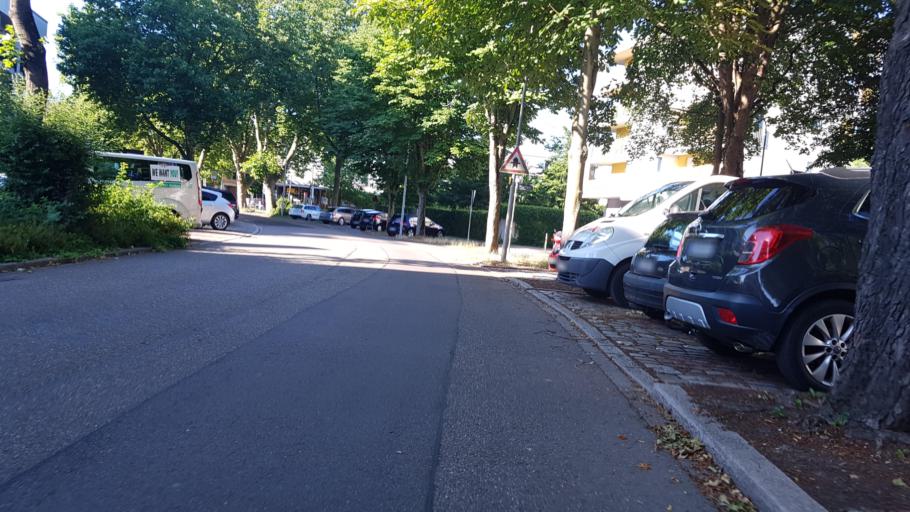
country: DE
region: Baden-Wuerttemberg
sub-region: Karlsruhe Region
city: Karlsruhe
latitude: 48.9986
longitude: 8.4587
